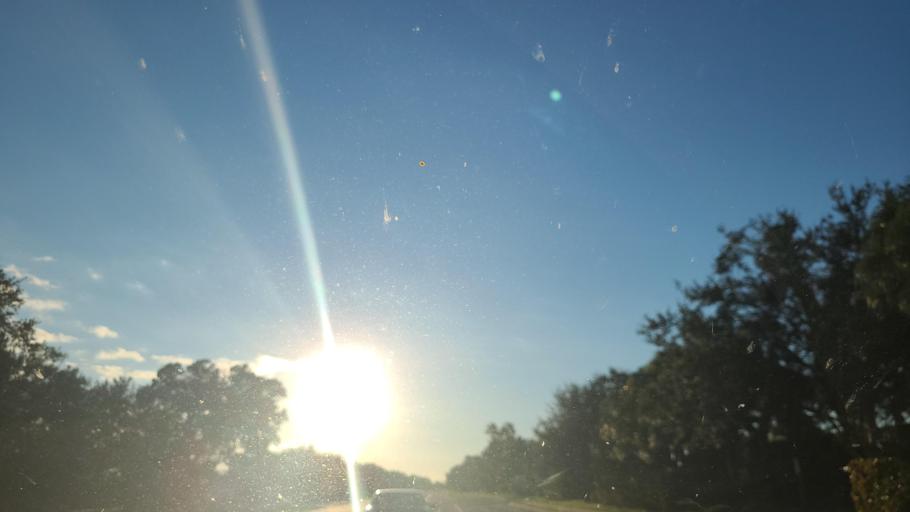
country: US
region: Florida
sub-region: Indian River County
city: Vero Beach South
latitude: 27.5944
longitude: -80.4415
